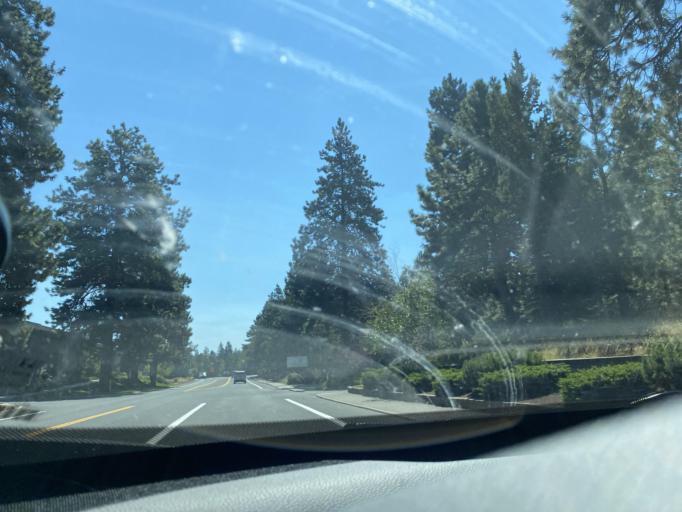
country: US
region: Oregon
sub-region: Deschutes County
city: Bend
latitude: 44.0632
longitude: -121.3412
